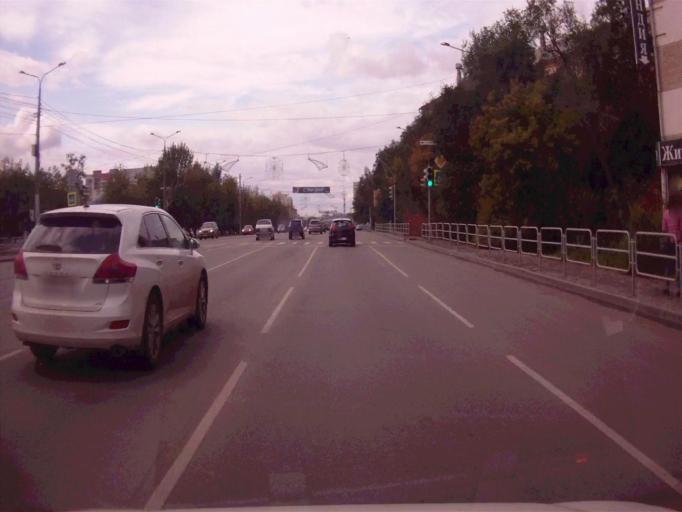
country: RU
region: Chelyabinsk
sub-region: Gorod Chelyabinsk
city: Chelyabinsk
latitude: 55.1396
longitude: 61.3979
